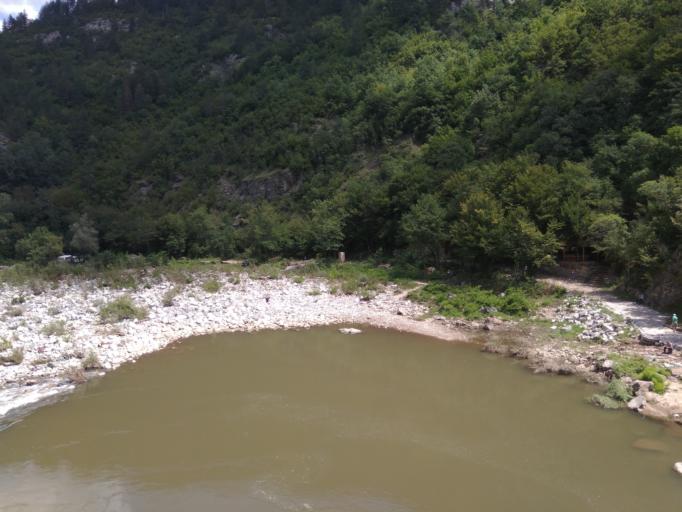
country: BG
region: Kurdzhali
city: Ardino
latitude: 41.6206
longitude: 25.1142
